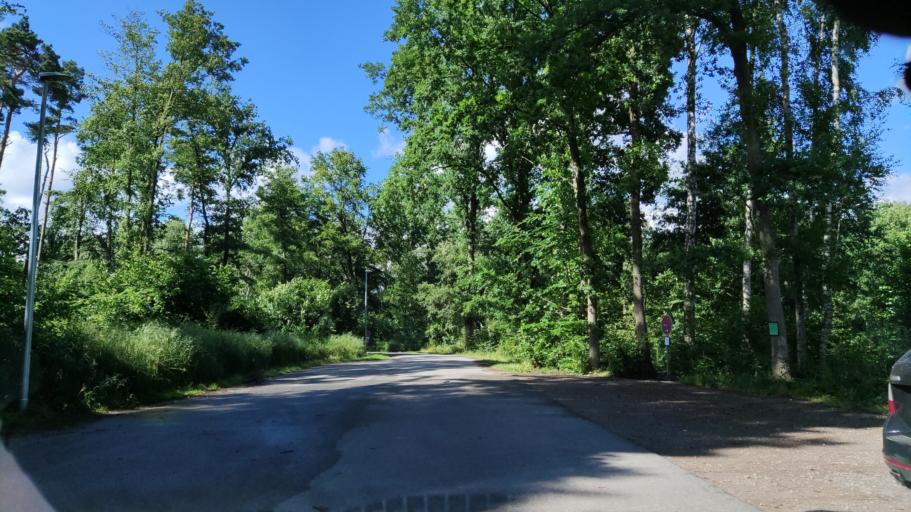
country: DE
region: Lower Saxony
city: Amelinghausen
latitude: 53.1302
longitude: 10.2304
